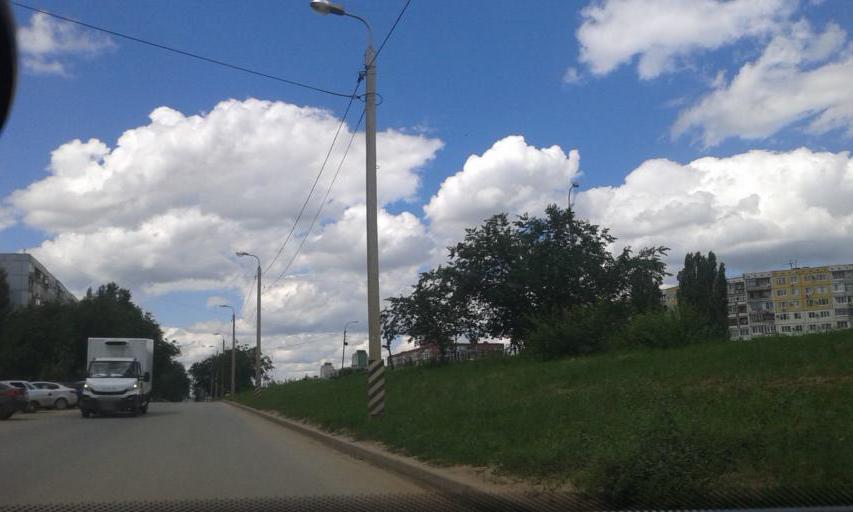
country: RU
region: Volgograd
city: Volgograd
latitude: 48.7485
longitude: 44.5064
